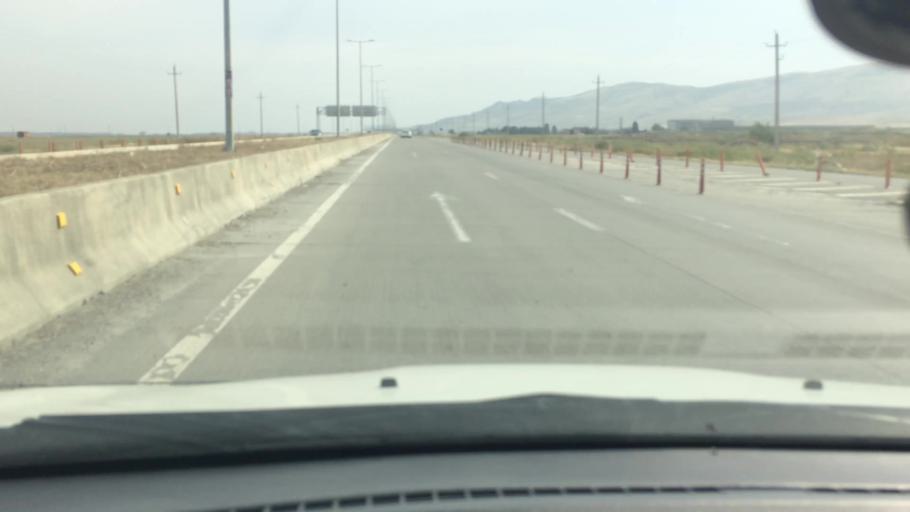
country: GE
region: Kvemo Kartli
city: Rust'avi
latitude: 41.6008
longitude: 44.9403
